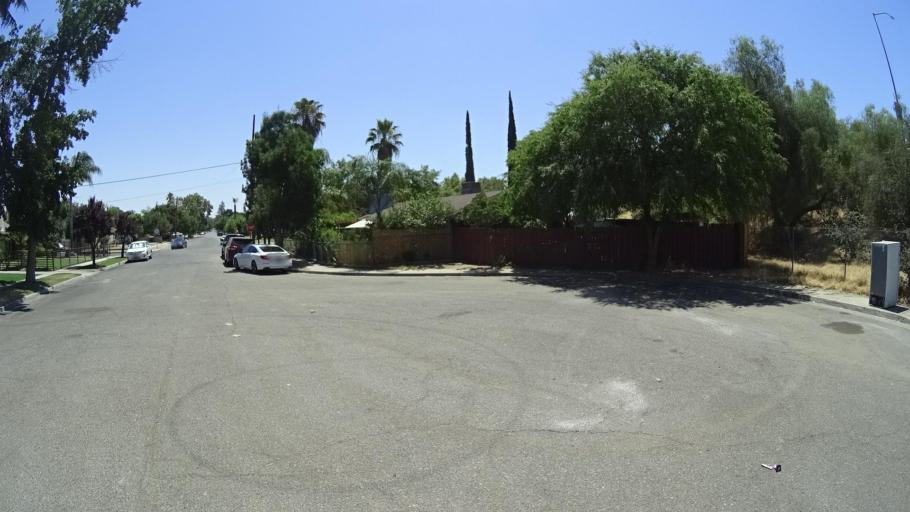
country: US
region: California
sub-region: Fresno County
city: Fresno
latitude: 36.7677
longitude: -119.7800
